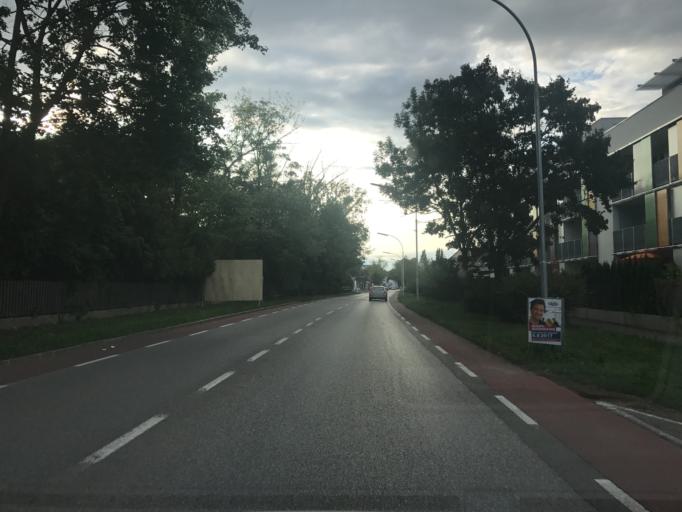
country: AT
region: Lower Austria
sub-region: Wiener Neustadt Stadt
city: Wiener Neustadt
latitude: 47.8086
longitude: 16.2583
